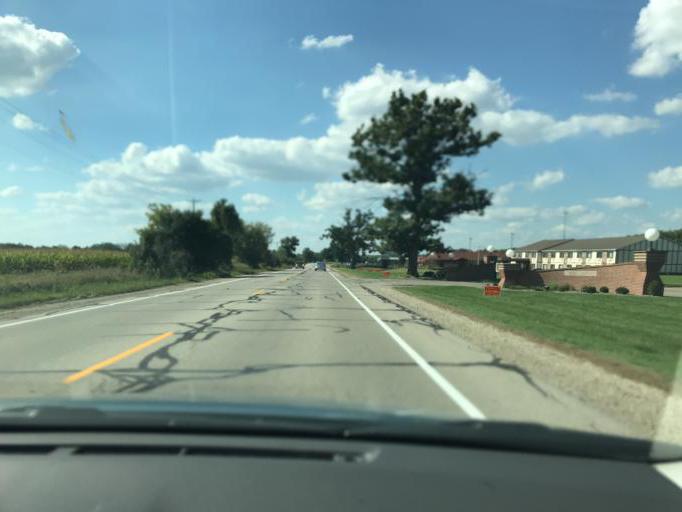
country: US
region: Wisconsin
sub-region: Walworth County
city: Williams Bay
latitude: 42.6141
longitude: -88.5719
